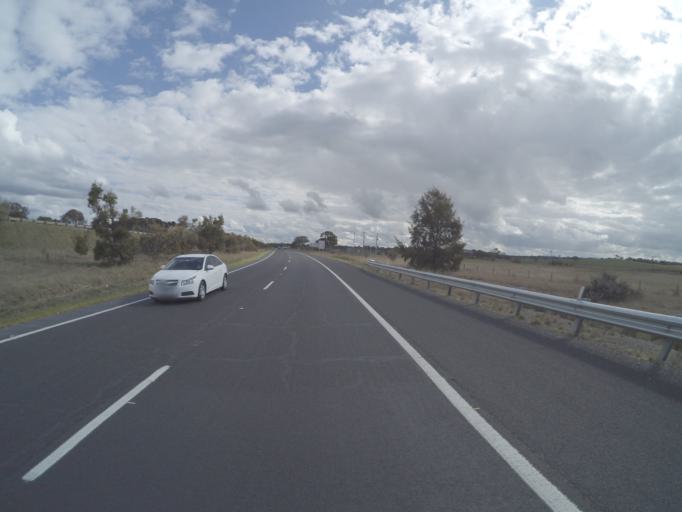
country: AU
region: New South Wales
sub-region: Goulburn Mulwaree
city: Goulburn
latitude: -34.7875
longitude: 149.6259
